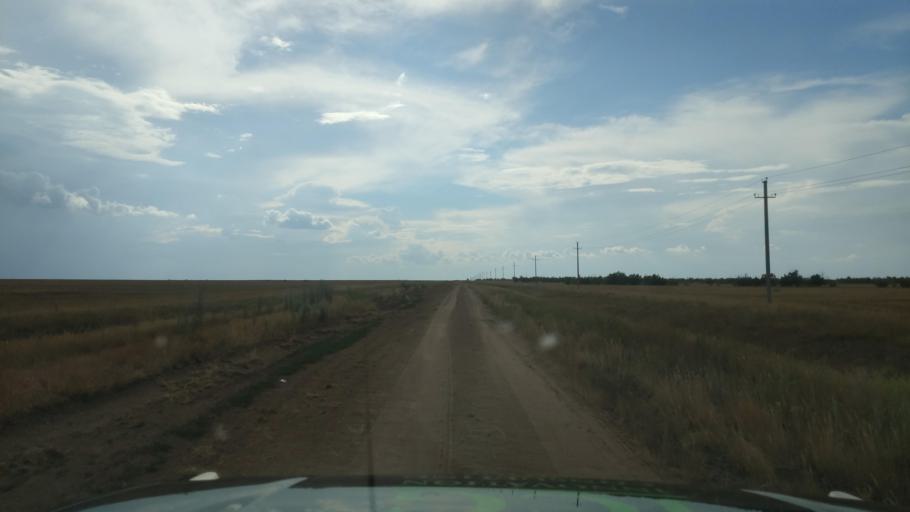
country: KZ
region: Pavlodar
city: Pavlodar
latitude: 52.5126
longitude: 77.5121
